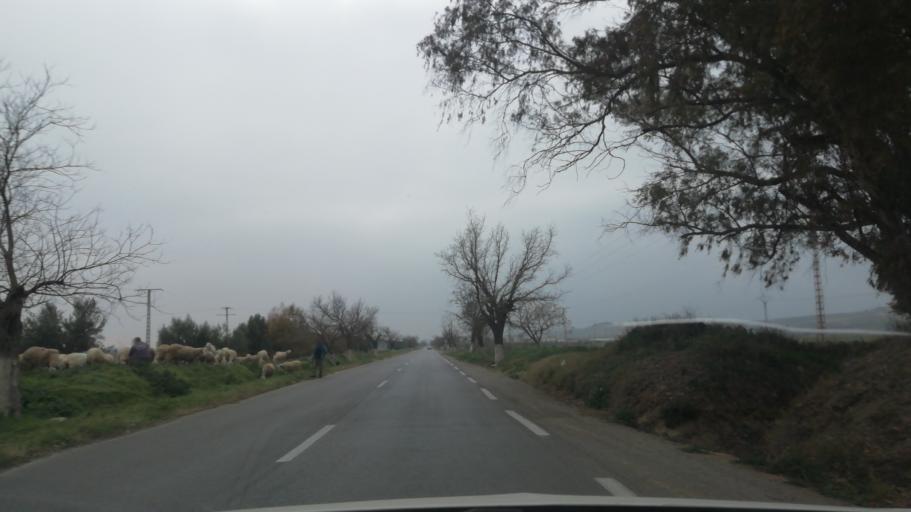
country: DZ
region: Sidi Bel Abbes
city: Sfizef
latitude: 35.2208
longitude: -0.2925
